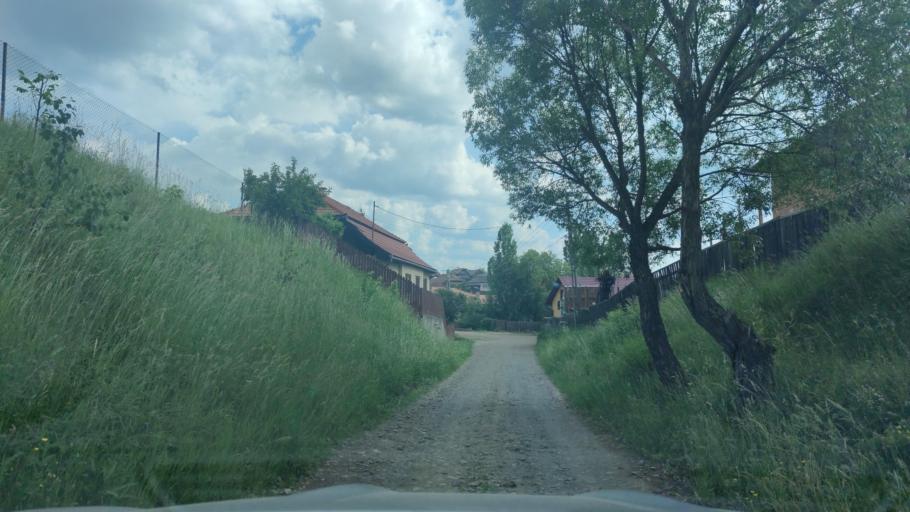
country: RO
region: Harghita
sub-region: Comuna Remetea
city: Remetea
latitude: 46.7948
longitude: 25.4460
